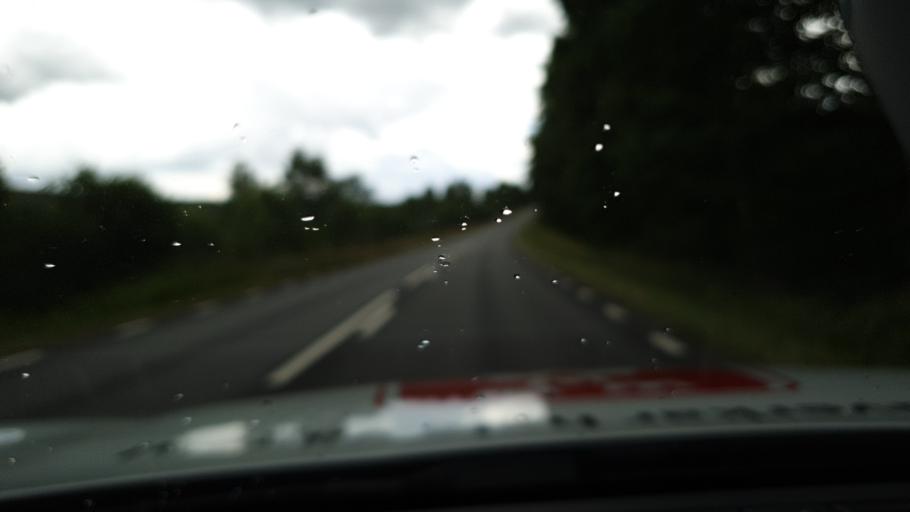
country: SE
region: Skane
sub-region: Hassleholms Kommun
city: Tormestorp
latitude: 56.1006
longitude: 13.7380
